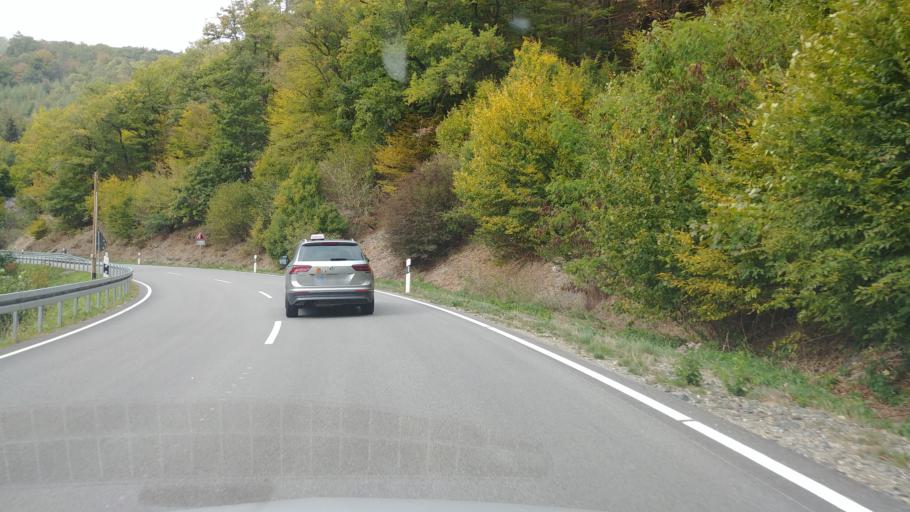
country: DE
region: Rheinland-Pfalz
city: Reckenroth
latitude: 50.2148
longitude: 8.0380
